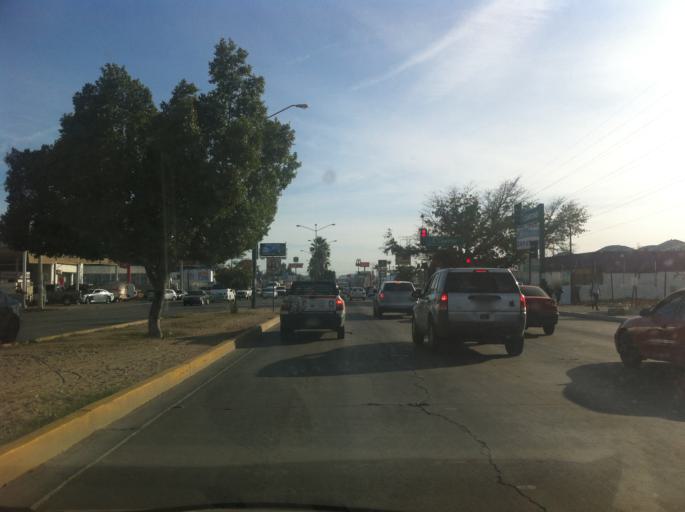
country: MX
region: Sonora
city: Hermosillo
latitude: 29.1044
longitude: -110.9925
